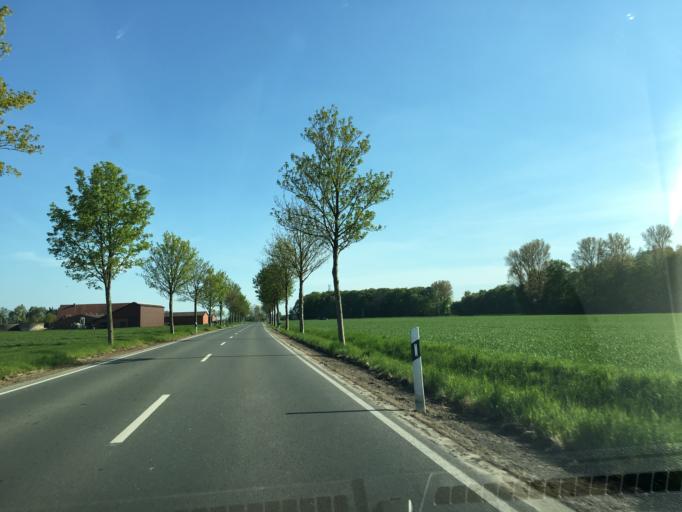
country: DE
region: North Rhine-Westphalia
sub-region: Regierungsbezirk Munster
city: Nordkirchen
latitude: 51.7938
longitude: 7.5391
